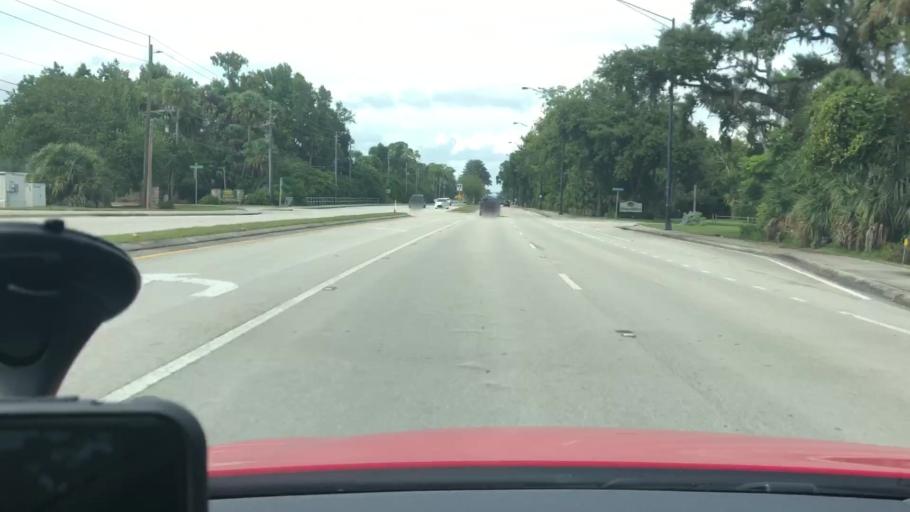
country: US
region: Florida
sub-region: Volusia County
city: Port Orange
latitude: 29.1207
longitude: -81.0012
